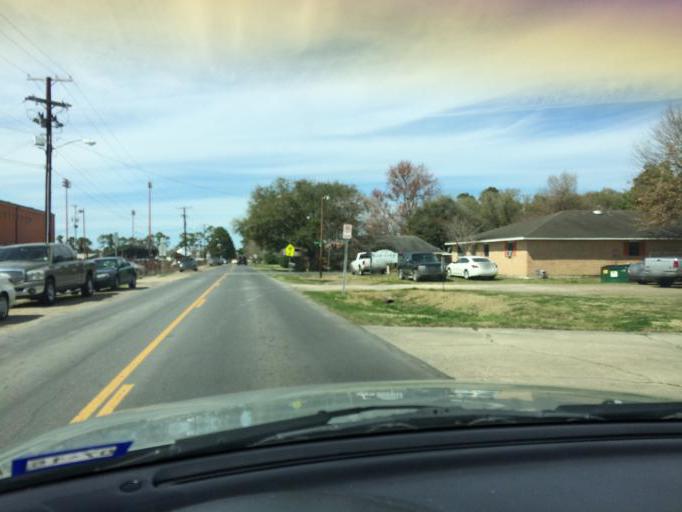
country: US
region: Louisiana
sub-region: Lafayette Parish
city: Lafayette
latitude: 30.2084
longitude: -92.0577
